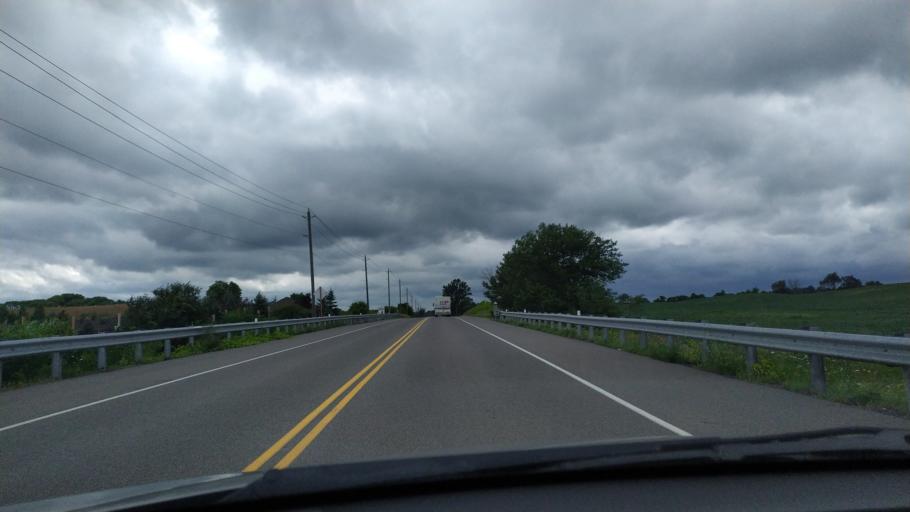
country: CA
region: Ontario
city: Kitchener
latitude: 43.3625
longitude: -80.4552
